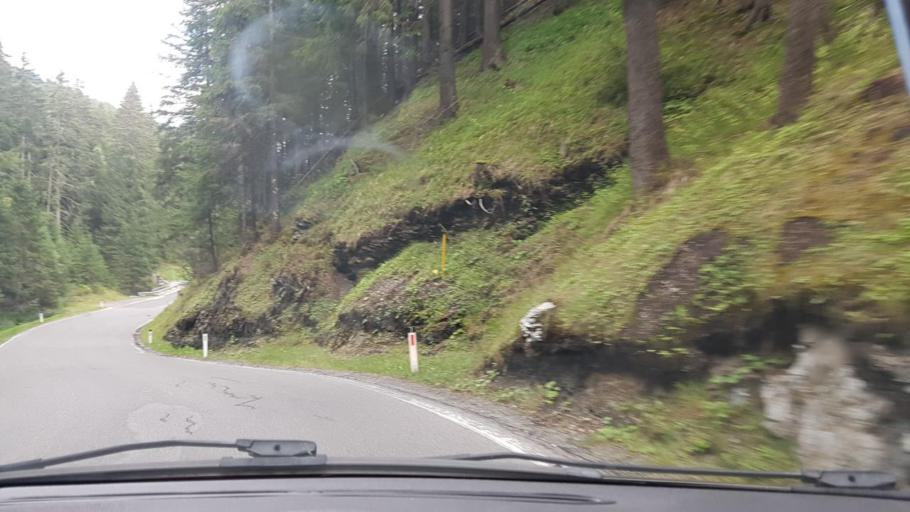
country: AT
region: Salzburg
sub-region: Politischer Bezirk Tamsweg
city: Sankt Michael im Lungau
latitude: 47.0489
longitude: 13.6167
